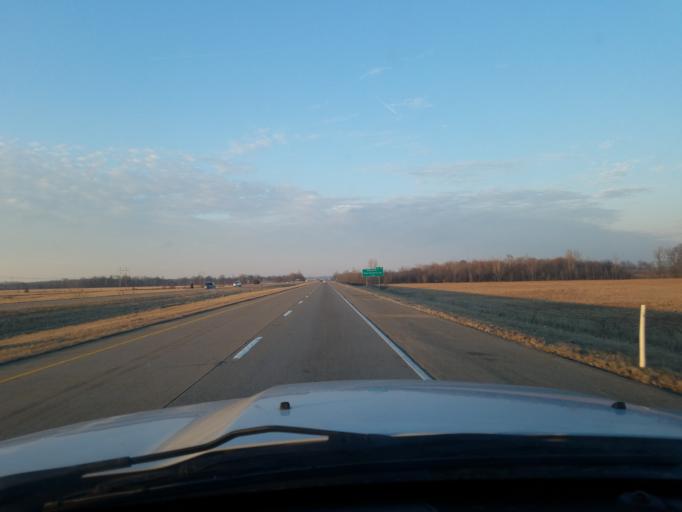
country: US
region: Indiana
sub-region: Vanderburgh County
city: Melody Hill
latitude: 38.0671
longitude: -87.4756
